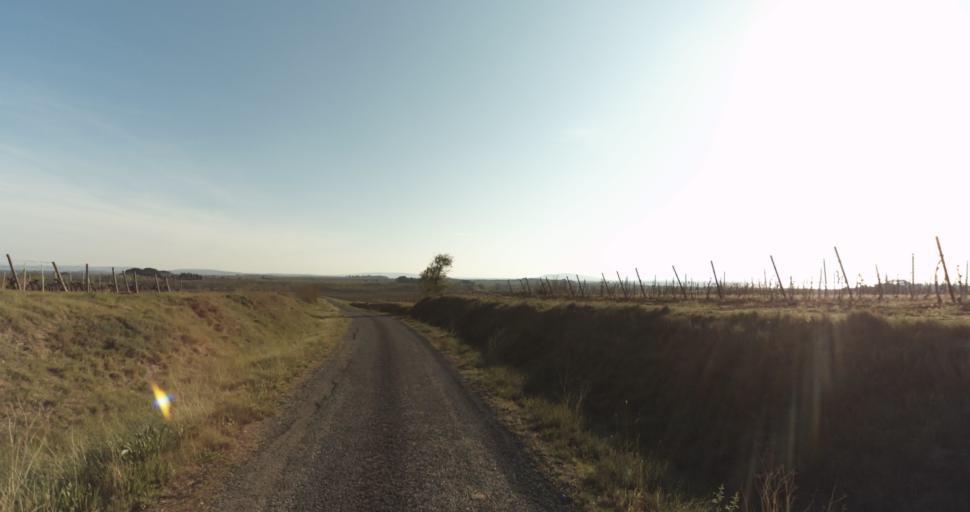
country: FR
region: Languedoc-Roussillon
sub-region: Departement de l'Herault
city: Marseillan
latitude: 43.3792
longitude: 3.5289
